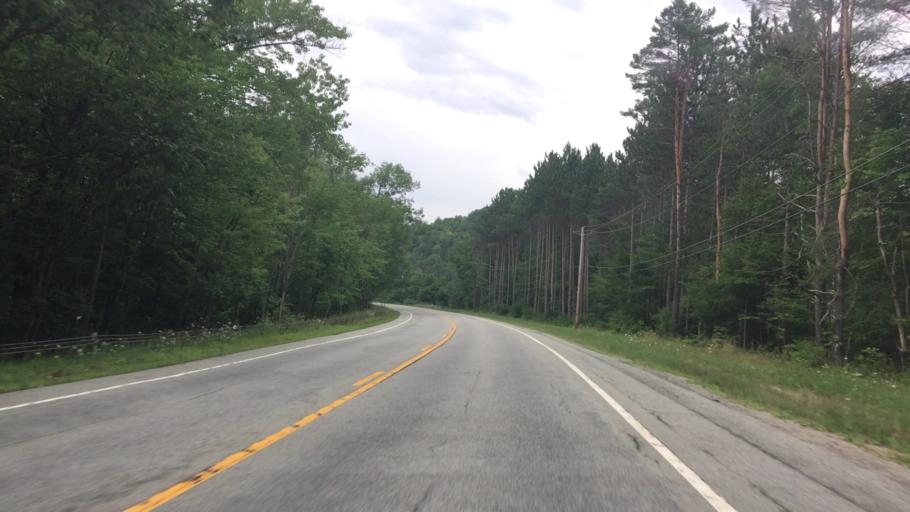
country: US
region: New York
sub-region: Essex County
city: Lake Placid
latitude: 44.2671
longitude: -73.7912
